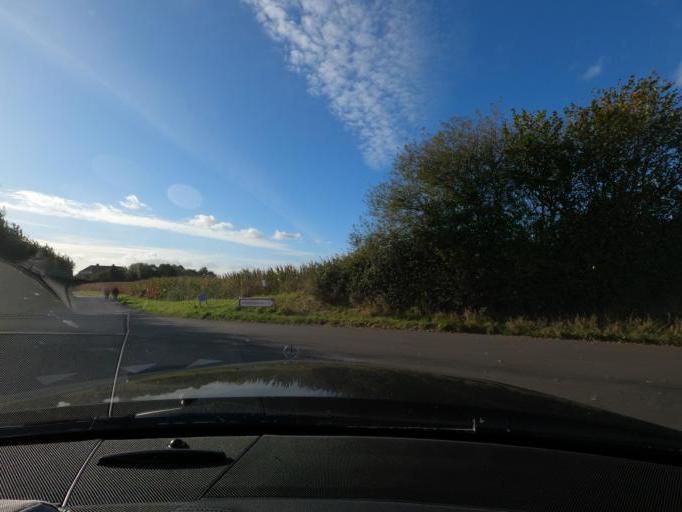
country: DK
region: South Denmark
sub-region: Sonderborg Kommune
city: Broager
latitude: 54.8805
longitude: 9.7082
